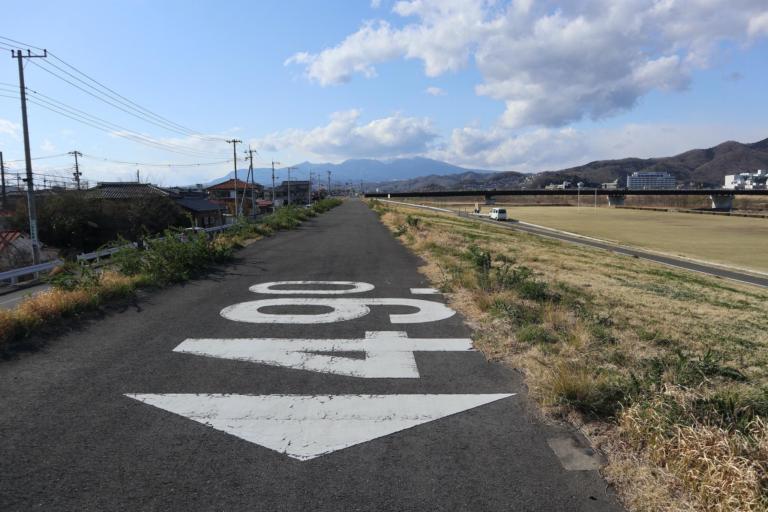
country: JP
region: Gunma
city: Kiryu
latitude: 36.3969
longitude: 139.3294
